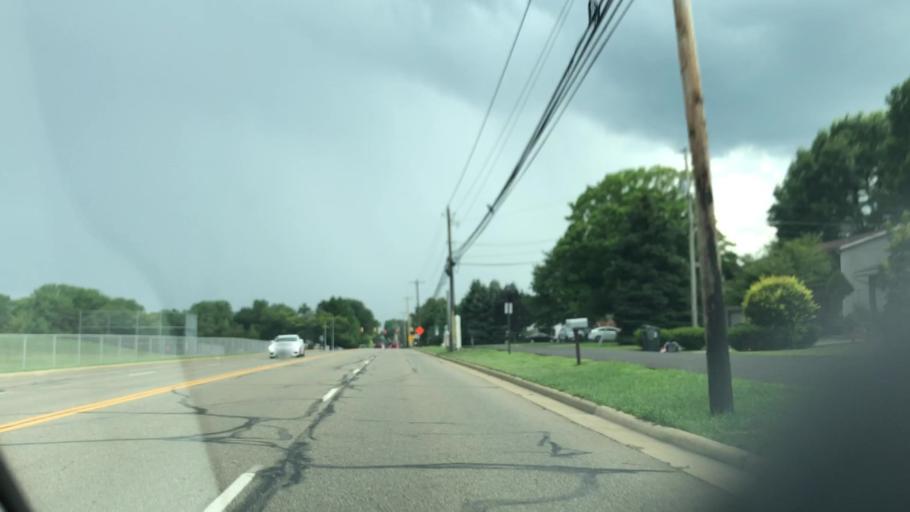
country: US
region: Ohio
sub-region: Stark County
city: North Canton
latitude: 40.8654
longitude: -81.4420
